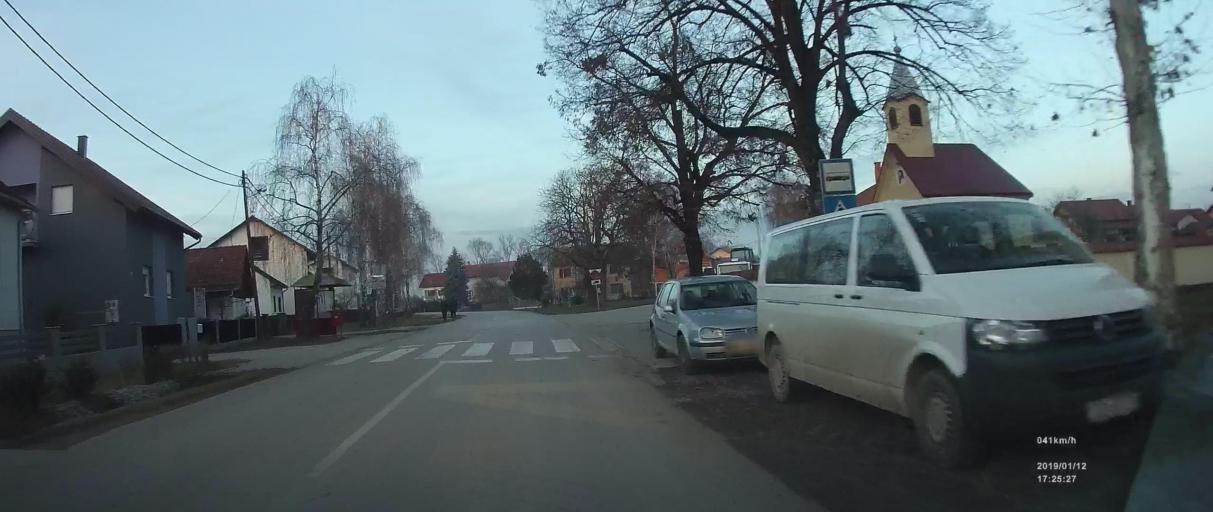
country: HR
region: Zagrebacka
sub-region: Grad Velika Gorica
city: Velika Gorica
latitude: 45.7317
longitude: 16.1012
